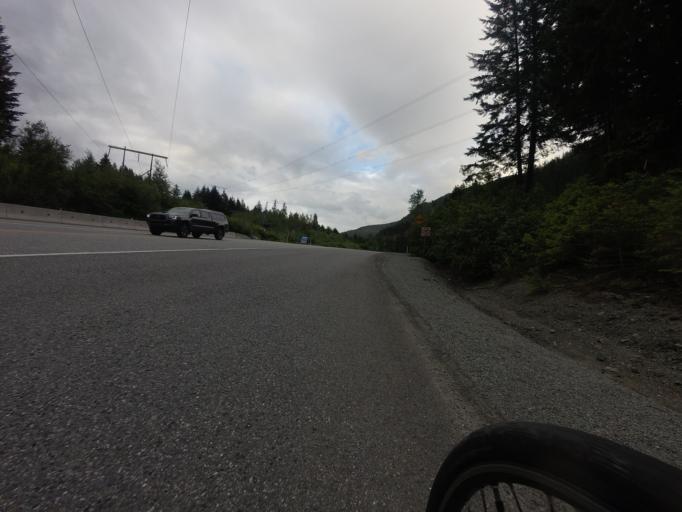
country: CA
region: British Columbia
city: Pemberton
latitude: 50.2872
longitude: -122.8456
